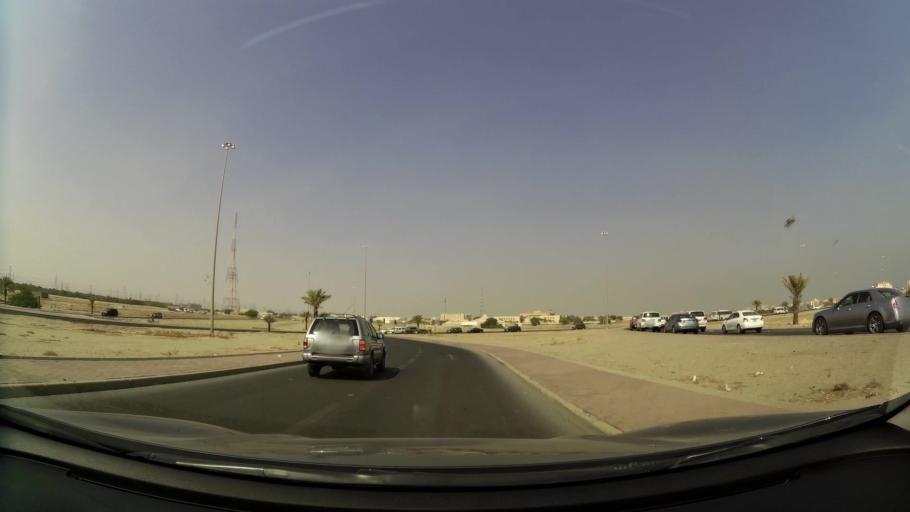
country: KW
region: Al Ahmadi
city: Al Fahahil
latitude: 29.0742
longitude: 48.1096
